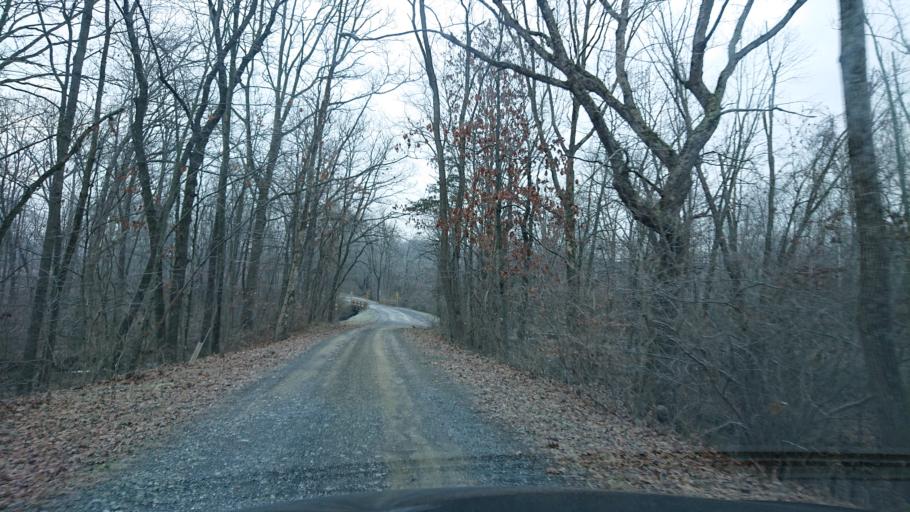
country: US
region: Pennsylvania
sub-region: Lebanon County
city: Palmyra
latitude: 40.4158
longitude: -76.5865
